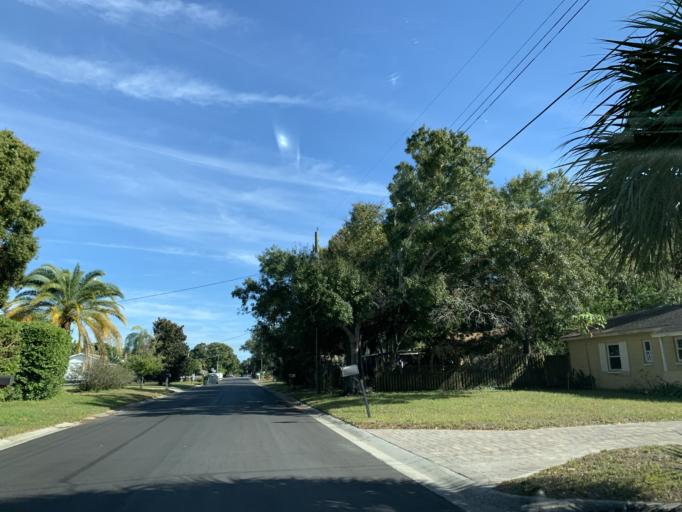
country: US
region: Florida
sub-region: Hillsborough County
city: Tampa
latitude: 27.8868
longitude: -82.5083
